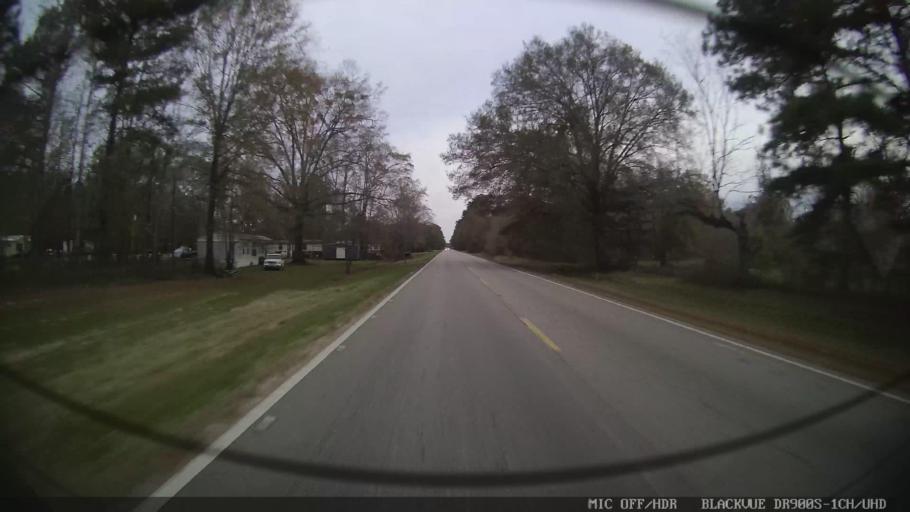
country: US
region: Mississippi
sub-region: Clarke County
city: Stonewall
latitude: 32.0288
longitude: -88.8638
